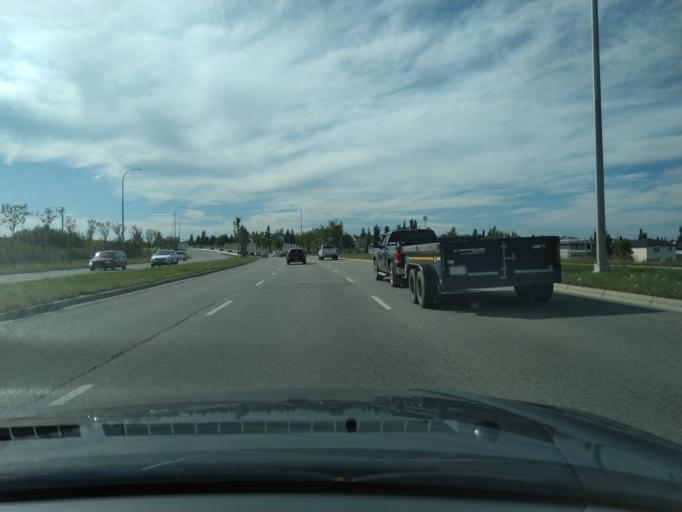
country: CA
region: Alberta
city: Calgary
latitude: 51.1428
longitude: -114.0454
